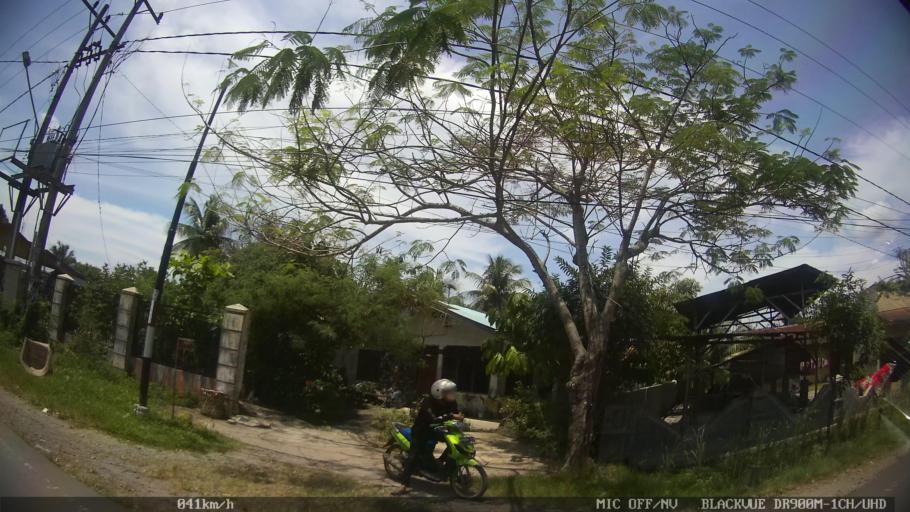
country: ID
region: North Sumatra
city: Binjai
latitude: 3.5938
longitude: 98.5027
